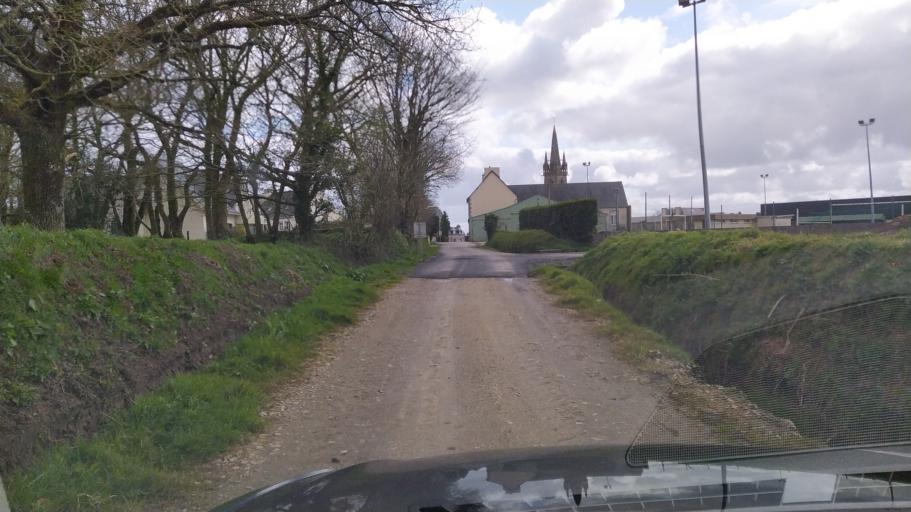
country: FR
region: Brittany
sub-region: Departement du Finistere
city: Bodilis
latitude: 48.5318
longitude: -4.1181
